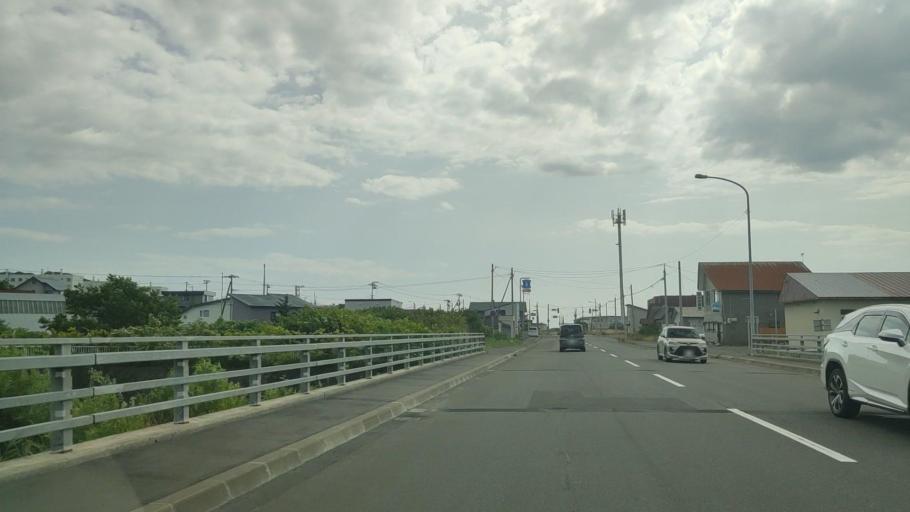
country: JP
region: Hokkaido
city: Rumoi
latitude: 44.1531
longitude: 141.6560
